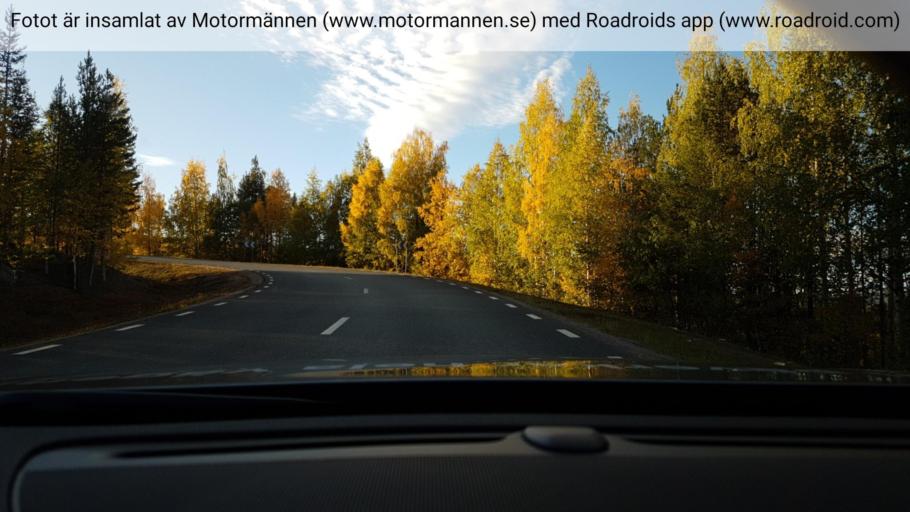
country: SE
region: Norrbotten
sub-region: Jokkmokks Kommun
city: Jokkmokk
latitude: 66.8114
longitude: 19.8747
